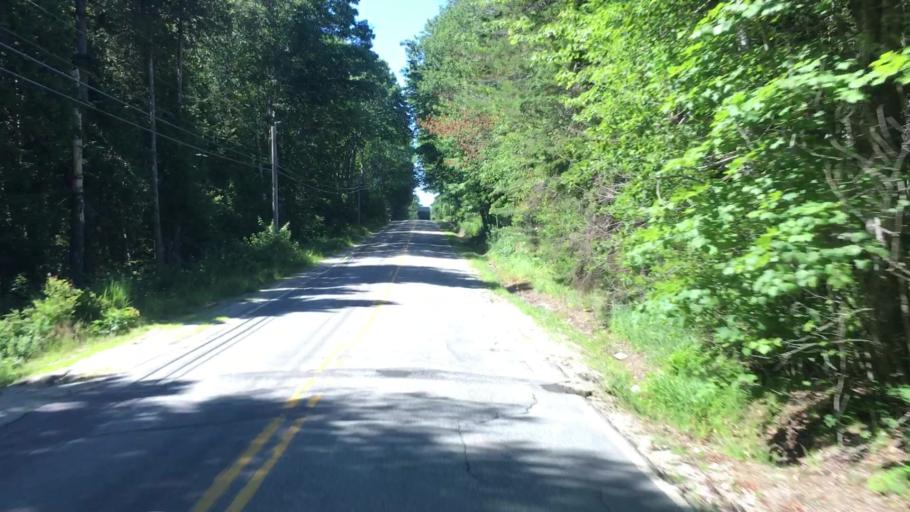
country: US
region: Maine
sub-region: Hancock County
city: Sedgwick
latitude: 44.3215
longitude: -68.6089
